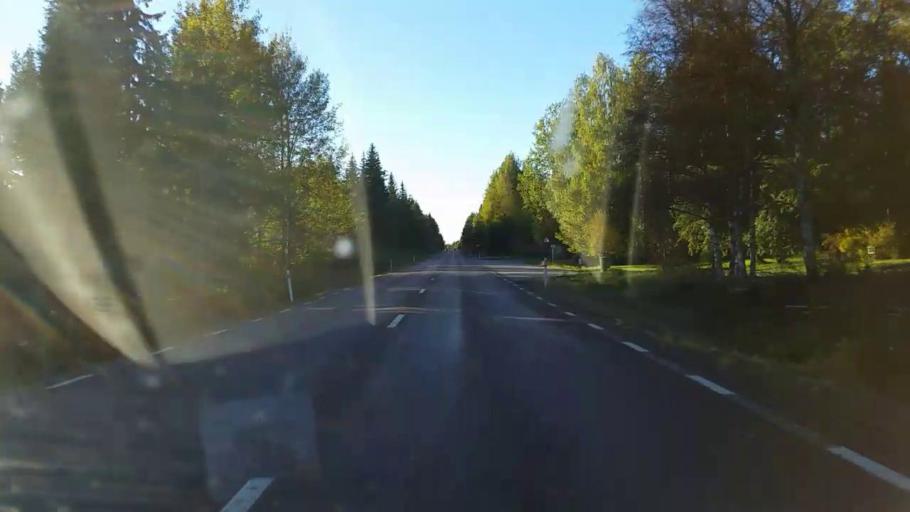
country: SE
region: Gaevleborg
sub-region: Ljusdals Kommun
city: Ljusdal
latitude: 61.8206
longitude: 16.1619
